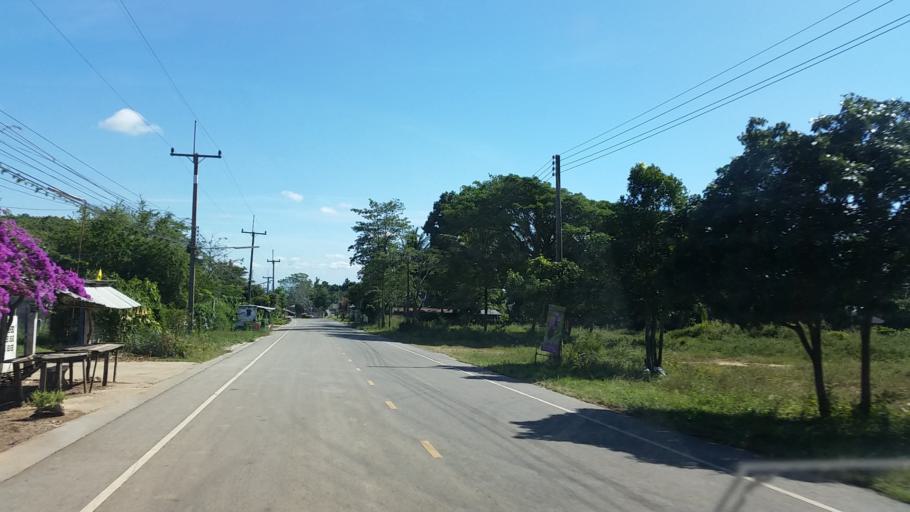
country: TH
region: Chaiyaphum
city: Sap Yai
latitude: 15.6273
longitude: 101.3973
